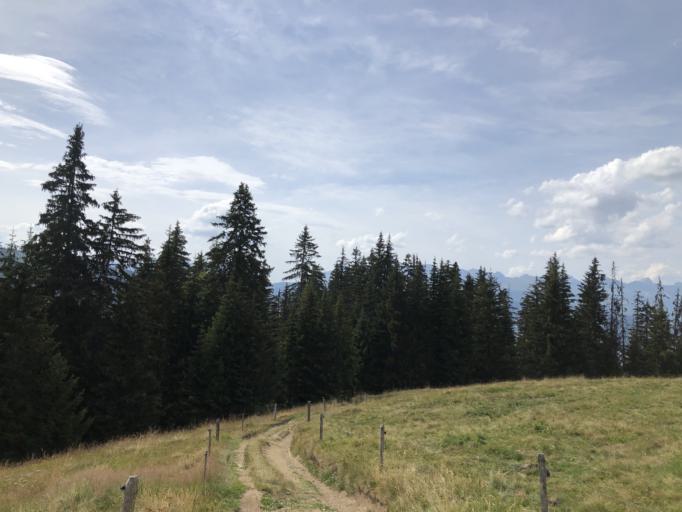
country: FR
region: Rhone-Alpes
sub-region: Departement de la Haute-Savoie
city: Megeve
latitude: 45.8236
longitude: 6.6610
